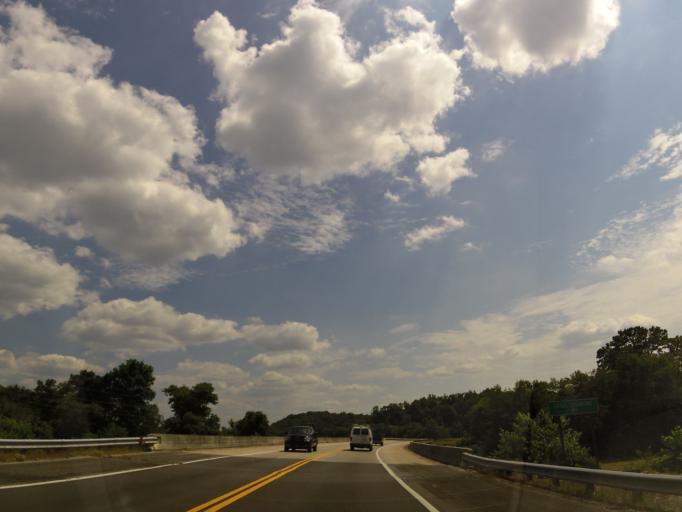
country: US
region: Tennessee
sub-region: Marion County
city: Jasper
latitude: 35.1049
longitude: -85.5759
